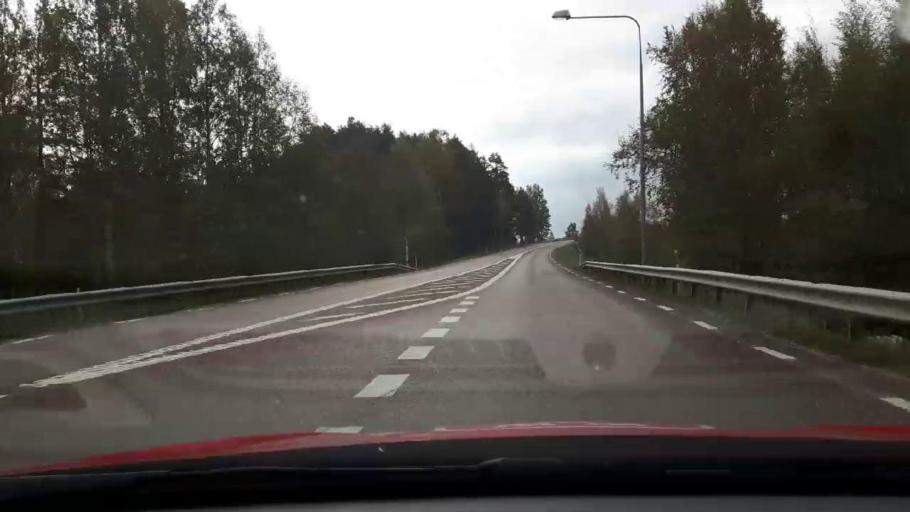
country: SE
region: Gaevleborg
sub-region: Bollnas Kommun
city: Kilafors
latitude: 61.2508
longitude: 16.5514
